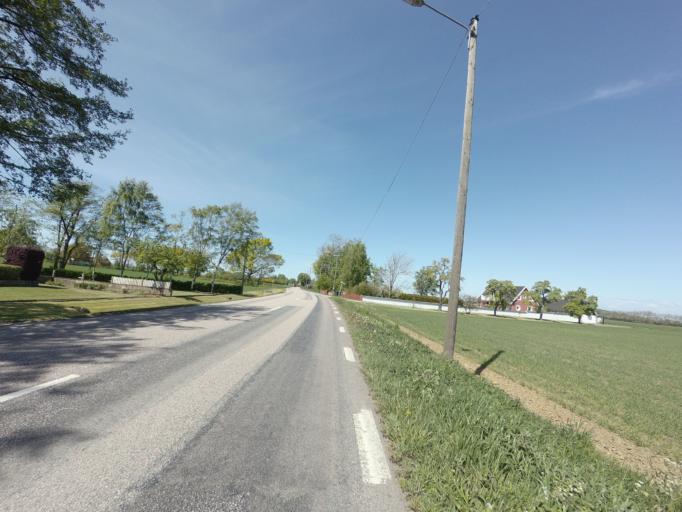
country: SE
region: Skane
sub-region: Helsingborg
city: Odakra
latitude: 56.1383
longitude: 12.6887
